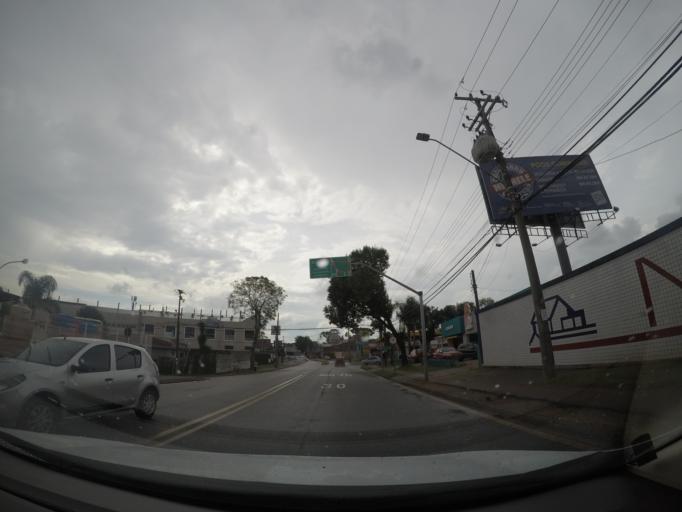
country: BR
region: Parana
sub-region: Sao Jose Dos Pinhais
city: Sao Jose dos Pinhais
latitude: -25.5196
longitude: -49.2552
